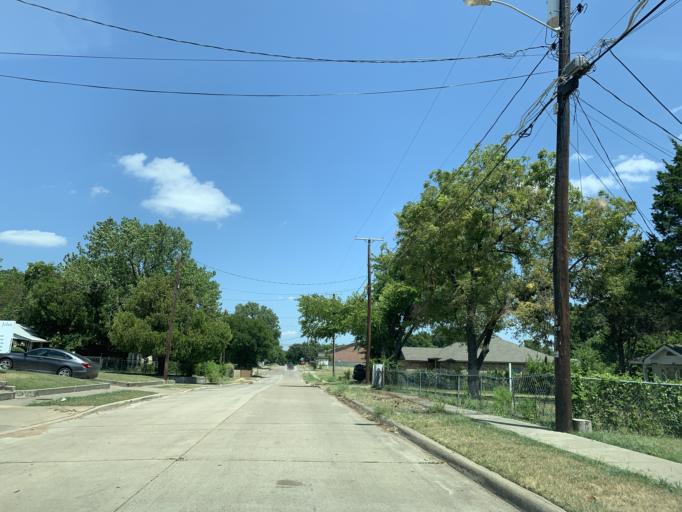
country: US
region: Texas
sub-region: Dallas County
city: Hutchins
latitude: 32.6880
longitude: -96.7800
